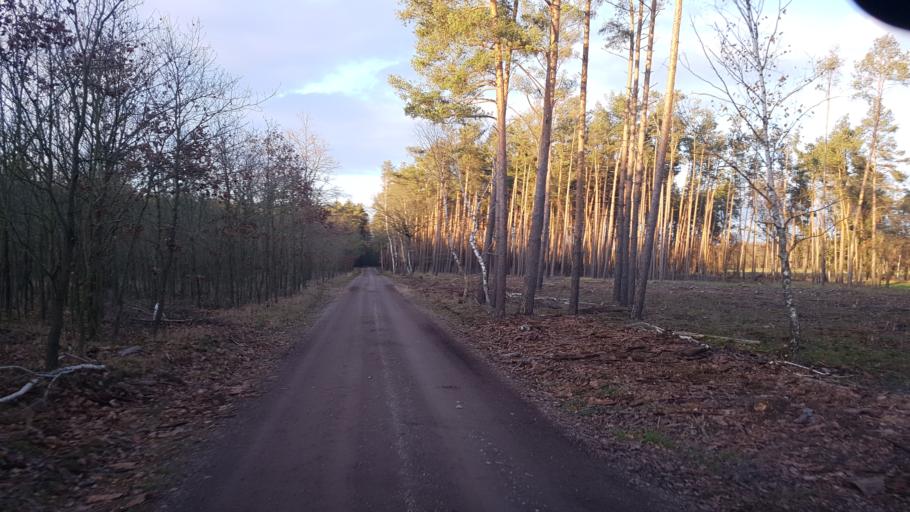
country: DE
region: Brandenburg
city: Falkenberg
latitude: 51.6212
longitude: 13.2804
